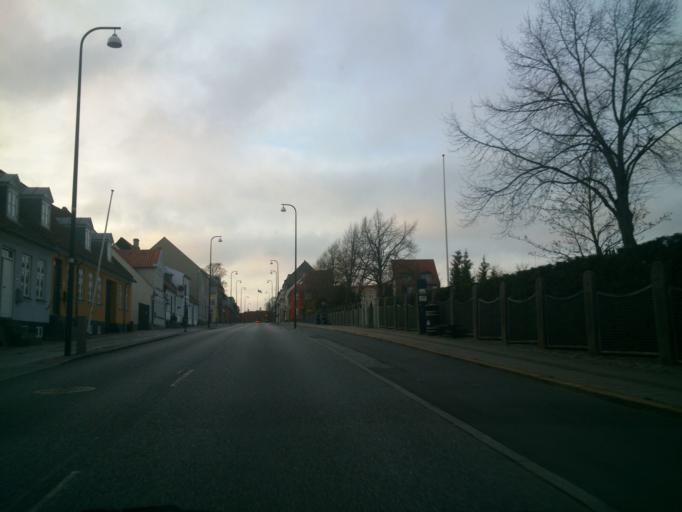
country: DK
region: South Denmark
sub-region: Fredericia Kommune
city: Fredericia
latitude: 55.5644
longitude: 9.7527
